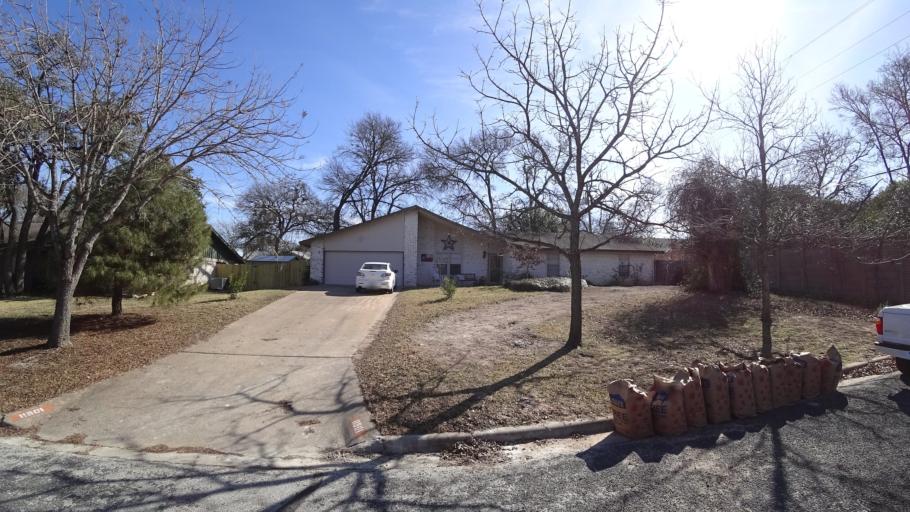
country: US
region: Texas
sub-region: Travis County
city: Wells Branch
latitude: 30.3848
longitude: -97.6876
